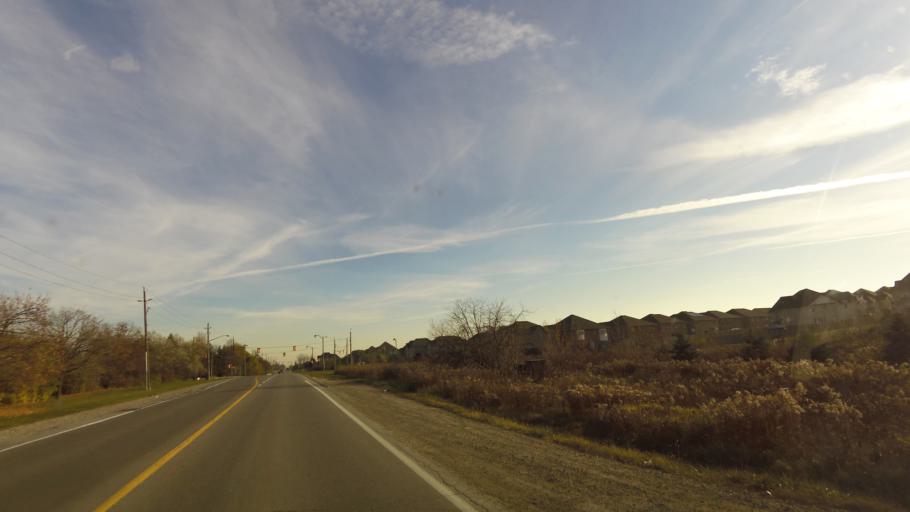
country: CA
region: Ontario
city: Brampton
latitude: 43.7889
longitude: -79.7329
